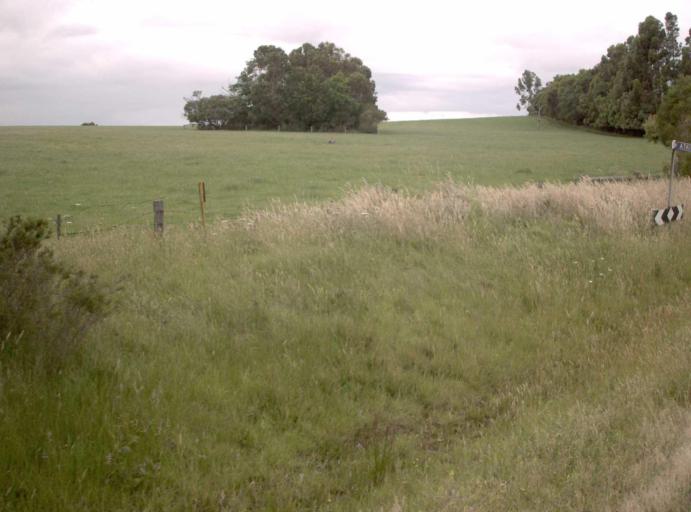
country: AU
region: Victoria
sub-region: Bass Coast
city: North Wonthaggi
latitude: -38.5503
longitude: 145.6553
